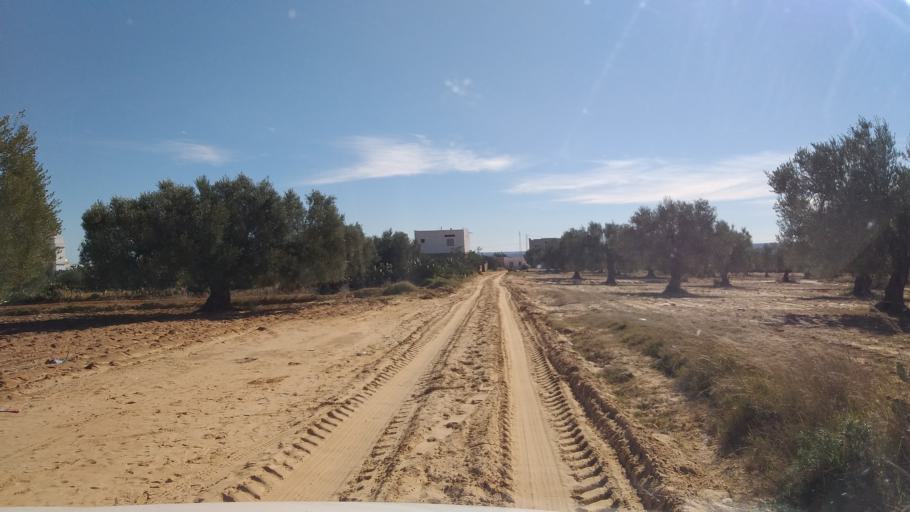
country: TN
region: Al Mahdiyah
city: El Jem
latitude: 35.2558
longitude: 10.6065
